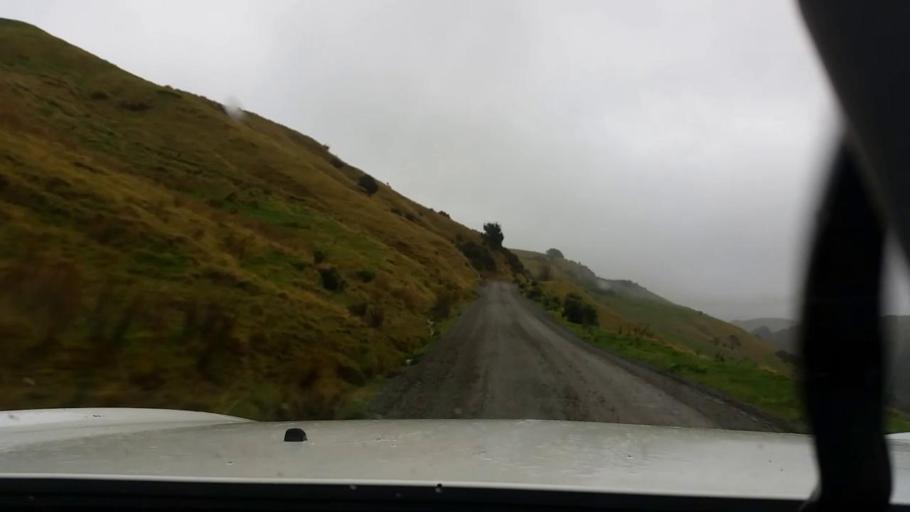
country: NZ
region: Wellington
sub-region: Masterton District
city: Masterton
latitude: -41.2499
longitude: 175.9108
